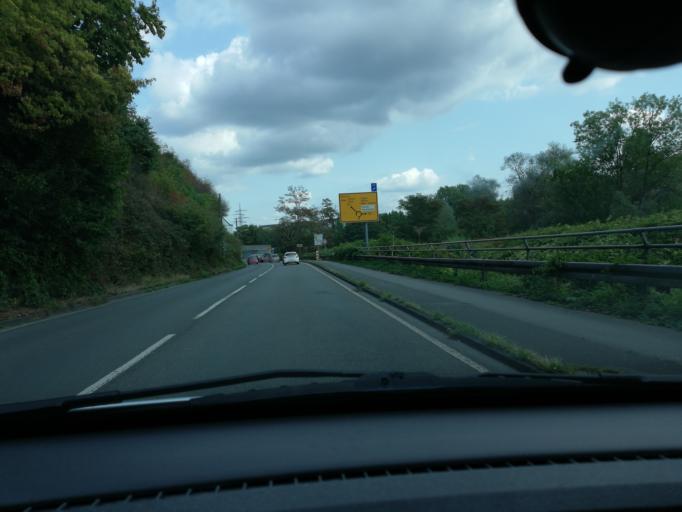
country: DE
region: North Rhine-Westphalia
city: Witten
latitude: 51.4351
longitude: 7.3146
